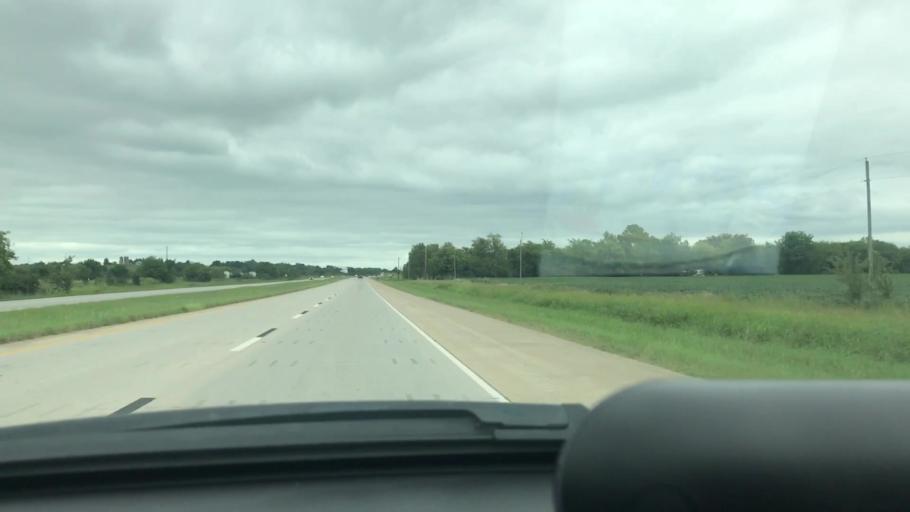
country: US
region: Oklahoma
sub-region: Mayes County
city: Chouteau
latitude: 36.0905
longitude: -95.3635
